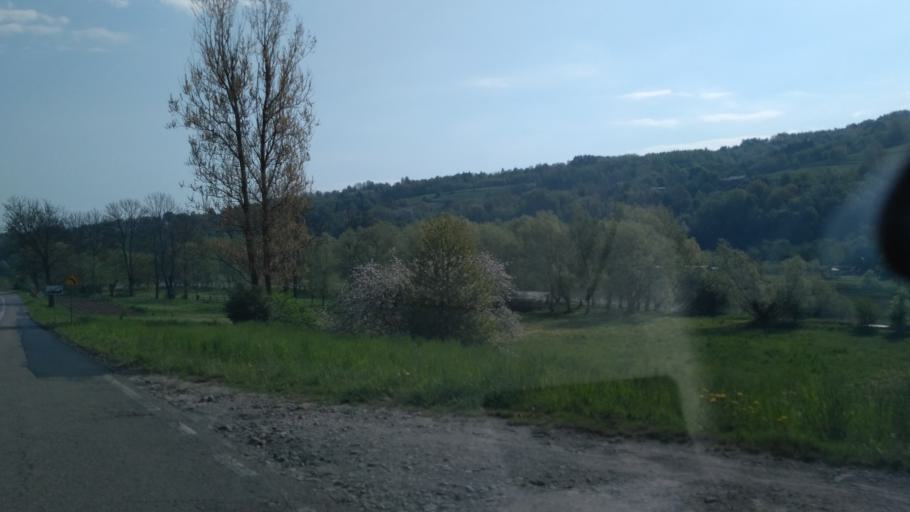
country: PL
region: Subcarpathian Voivodeship
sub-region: Powiat rzeszowski
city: Dynow
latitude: 49.7944
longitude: 22.2380
